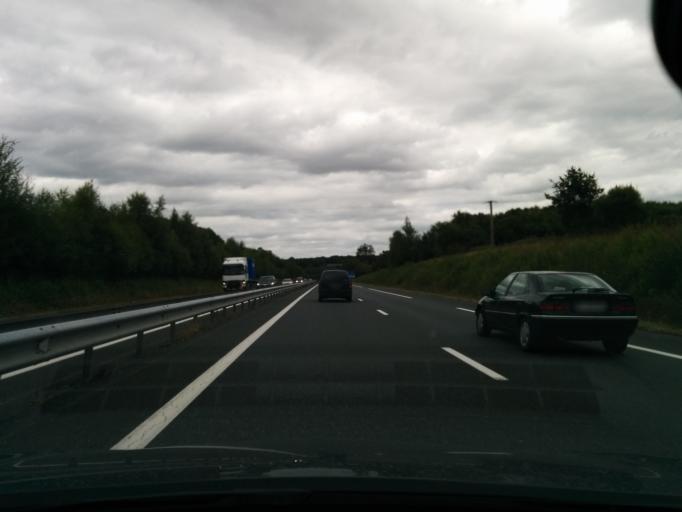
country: FR
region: Centre
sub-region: Departement de l'Indre
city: Chantome
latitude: 46.3998
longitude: 1.4549
